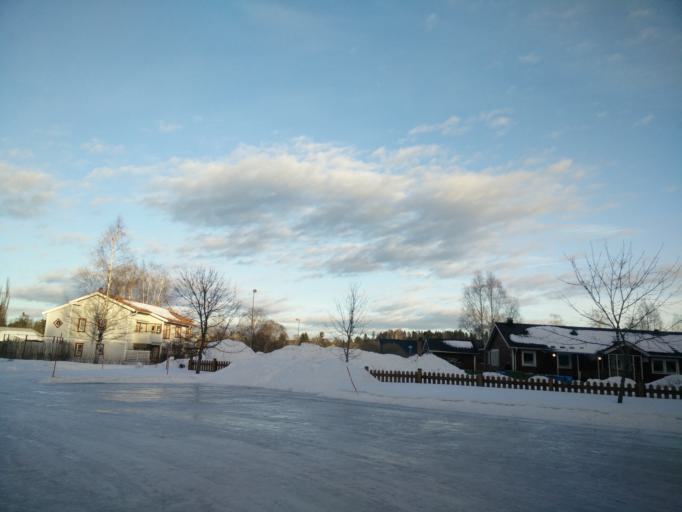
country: SE
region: Vaesternorrland
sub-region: Sundsvalls Kommun
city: Njurundabommen
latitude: 62.2646
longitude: 17.3722
